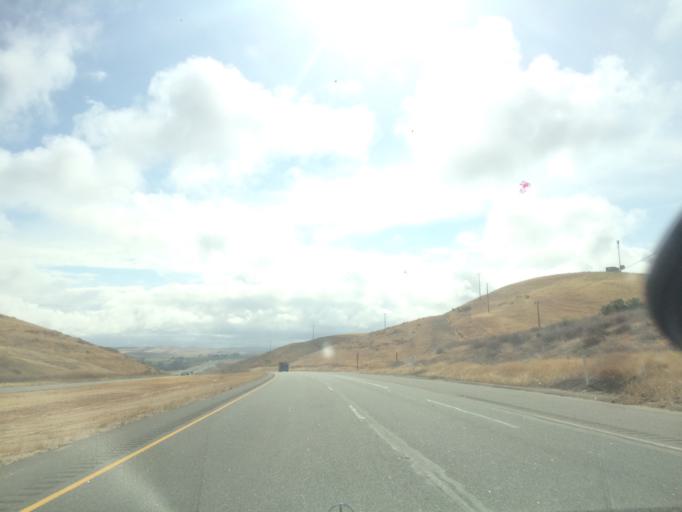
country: US
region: California
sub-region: San Luis Obispo County
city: Shandon
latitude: 35.6550
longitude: -120.5218
